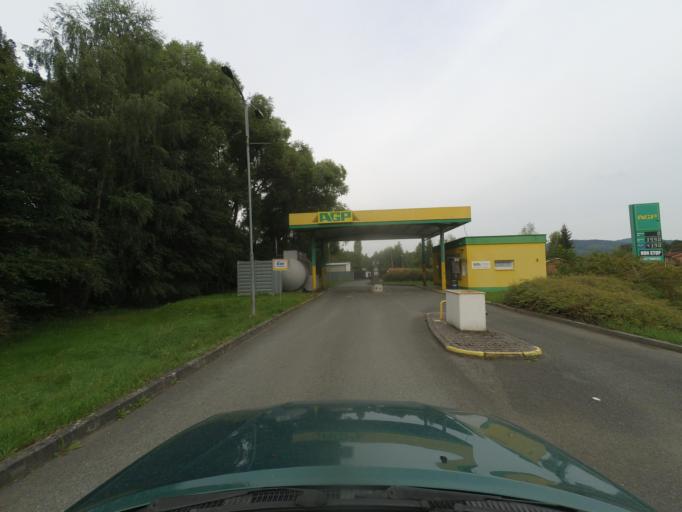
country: CZ
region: Plzensky
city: Bela nad Radbuzou
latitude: 49.5891
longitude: 12.7196
